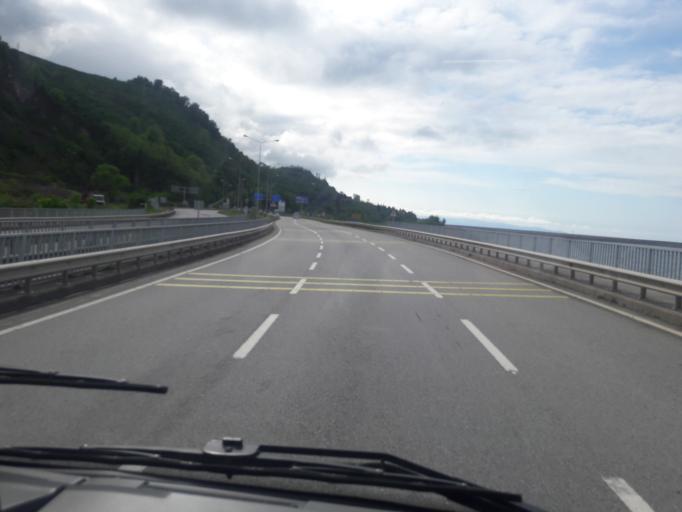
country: TR
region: Giresun
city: Piraziz
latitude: 40.9579
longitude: 38.1161
